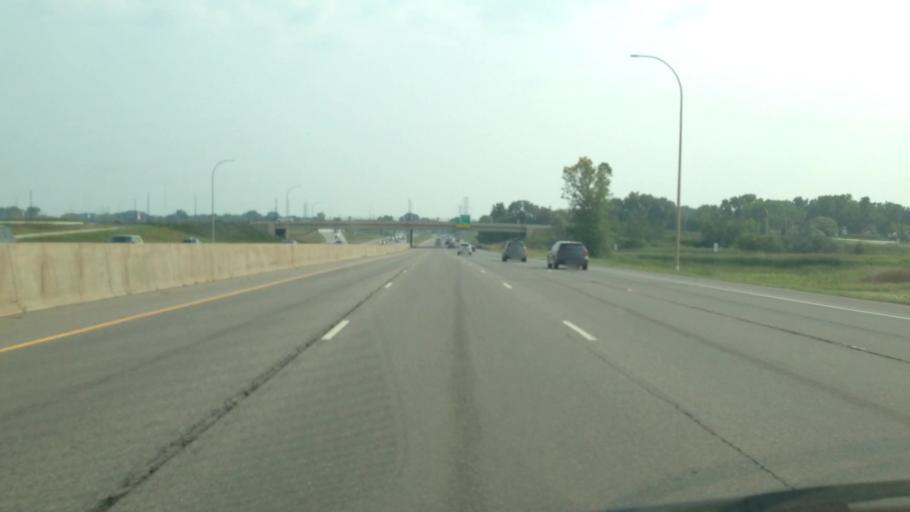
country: US
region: Minnesota
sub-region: Ramsey County
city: Mounds View
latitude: 45.0981
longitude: -93.1884
